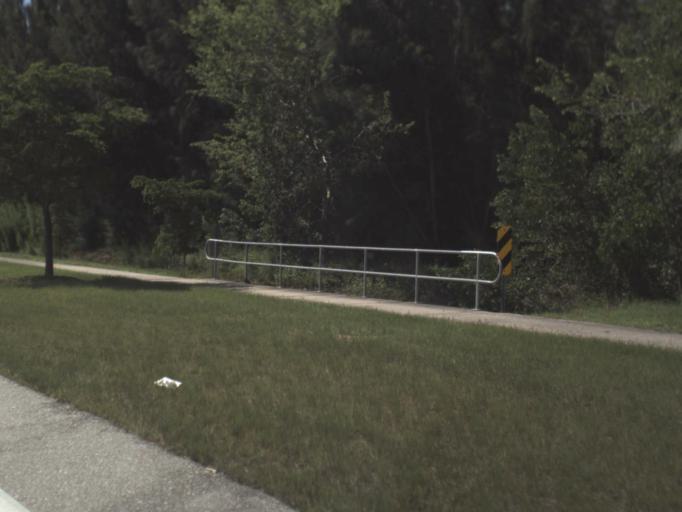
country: US
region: Florida
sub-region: Lee County
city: Pine Island Center
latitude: 26.6273
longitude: -82.0408
